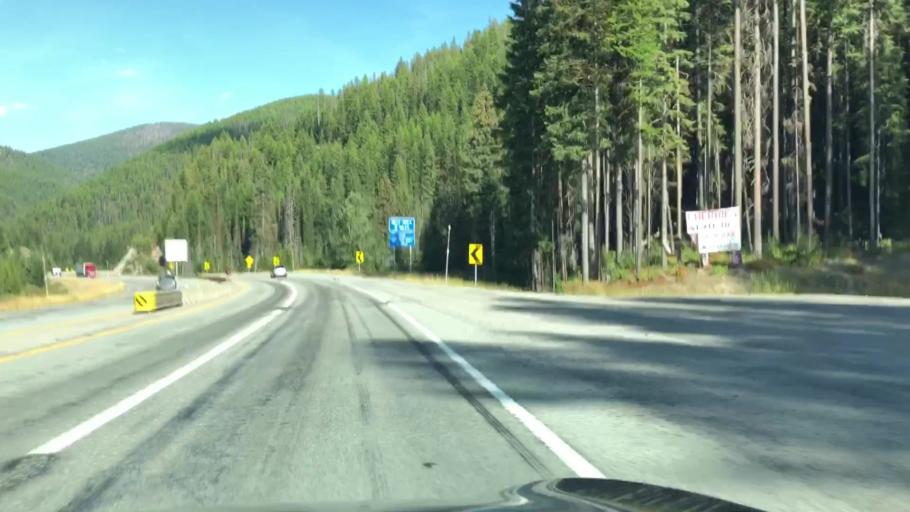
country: US
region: Idaho
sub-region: Shoshone County
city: Wallace
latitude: 47.4340
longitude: -115.6649
